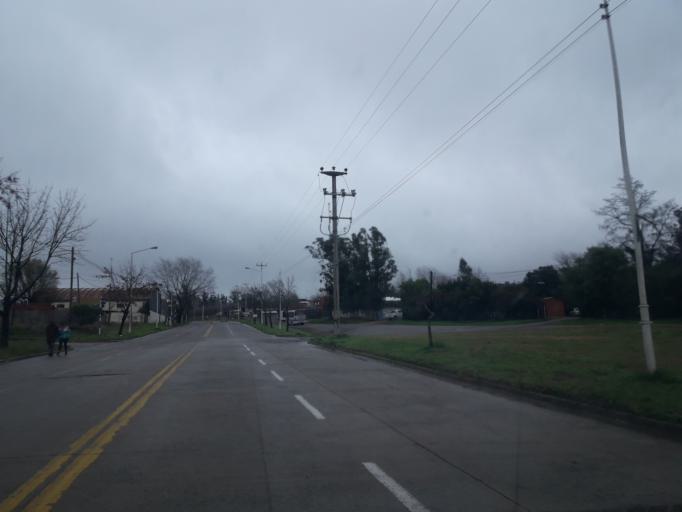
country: AR
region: Buenos Aires
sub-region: Partido de Tandil
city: Tandil
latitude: -37.3234
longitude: -59.1688
